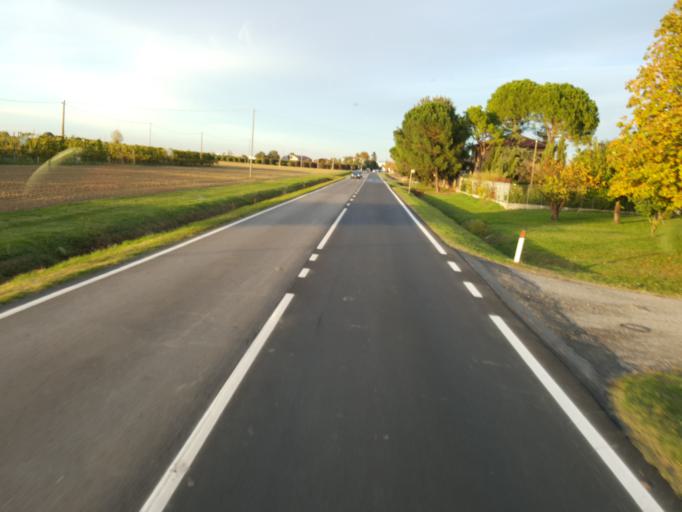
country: IT
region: Emilia-Romagna
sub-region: Provincia di Ravenna
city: Faenza
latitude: 44.3098
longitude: 11.8875
